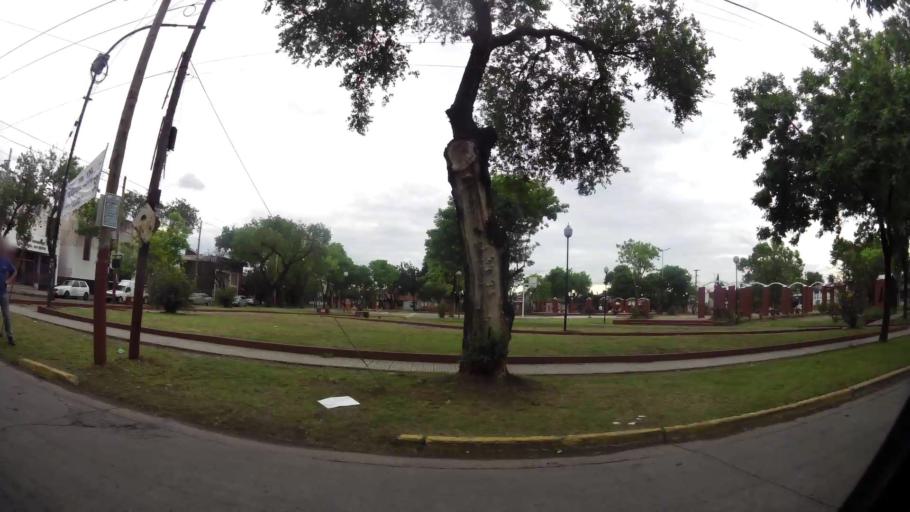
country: AR
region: Buenos Aires
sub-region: Partido de Lanus
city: Lanus
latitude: -34.7336
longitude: -58.3609
